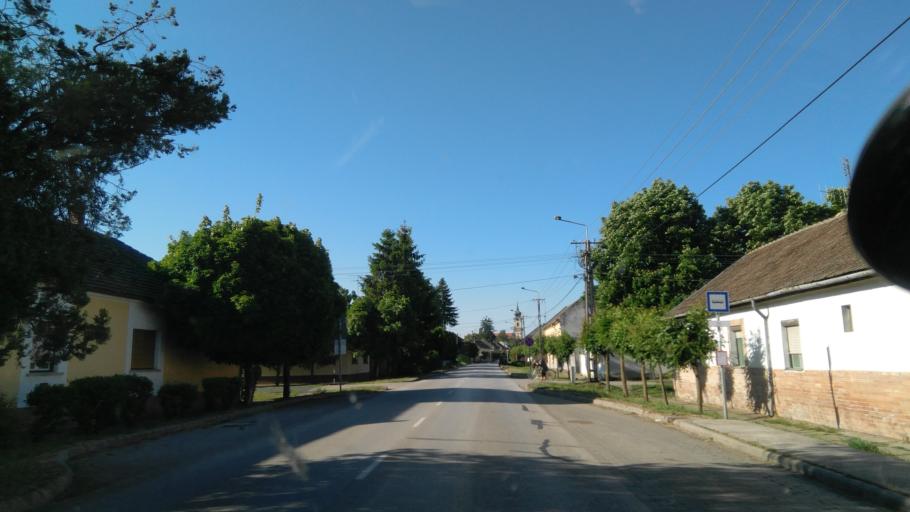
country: HU
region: Bekes
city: Elek
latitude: 46.5340
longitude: 21.2540
